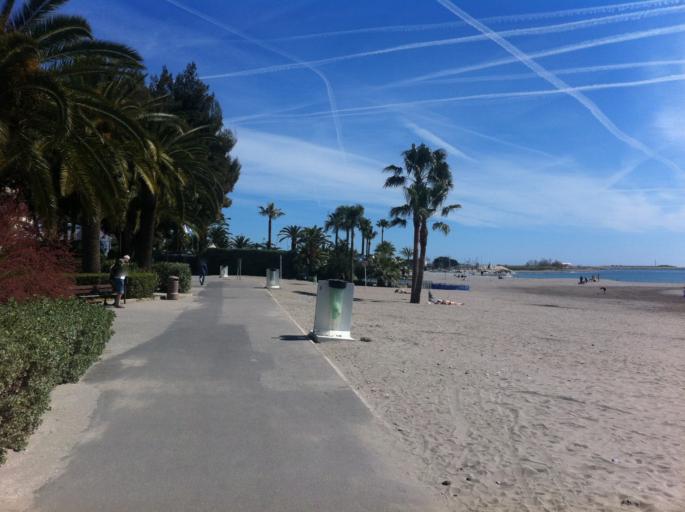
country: FR
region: Provence-Alpes-Cote d'Azur
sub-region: Departement des Alpes-Maritimes
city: Saint-Laurent-du-Var
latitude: 43.6581
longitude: 7.1937
